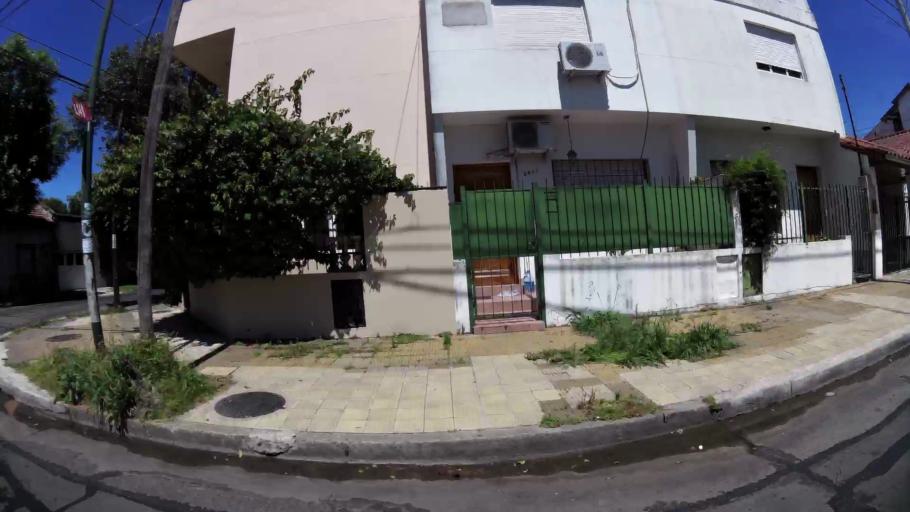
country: AR
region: Buenos Aires
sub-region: Partido de General San Martin
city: General San Martin
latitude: -34.5238
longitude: -58.5503
